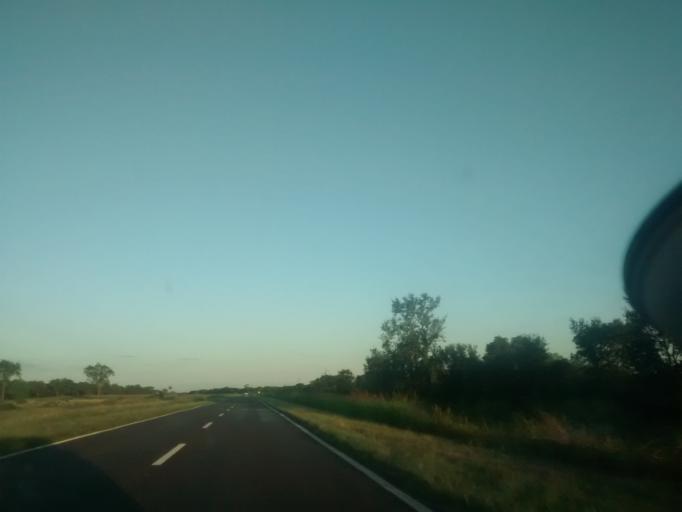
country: AR
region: Chaco
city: La Escondida
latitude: -27.1139
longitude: -59.5718
